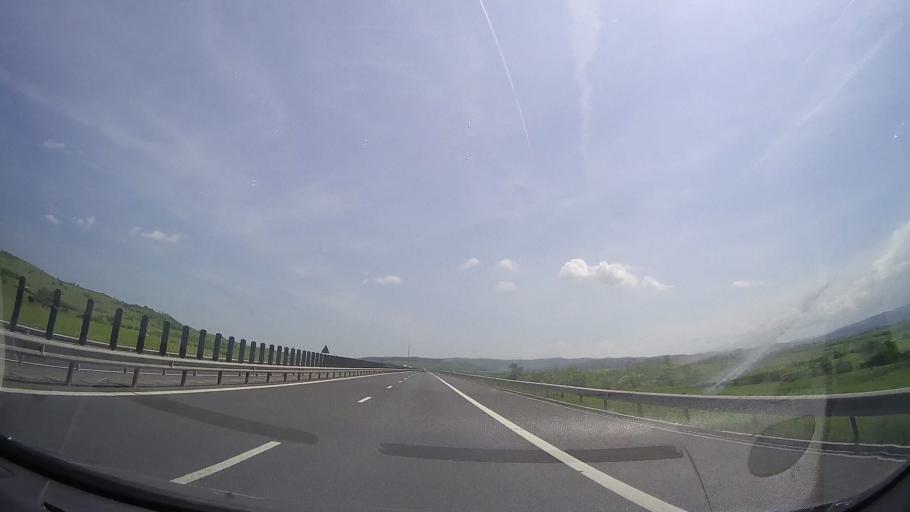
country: RO
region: Sibiu
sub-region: Oras Miercurea Sibiului
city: Miercurea Sibiului
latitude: 45.8946
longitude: 23.8147
